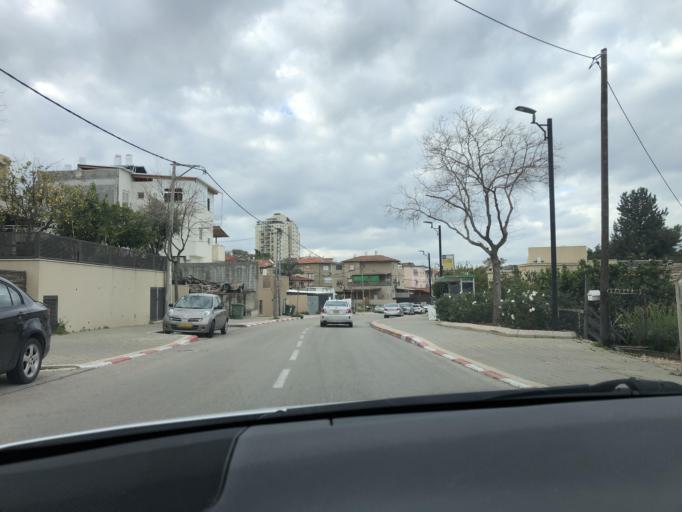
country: IL
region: Central District
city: Rosh Ha'Ayin
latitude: 32.0910
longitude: 34.9573
